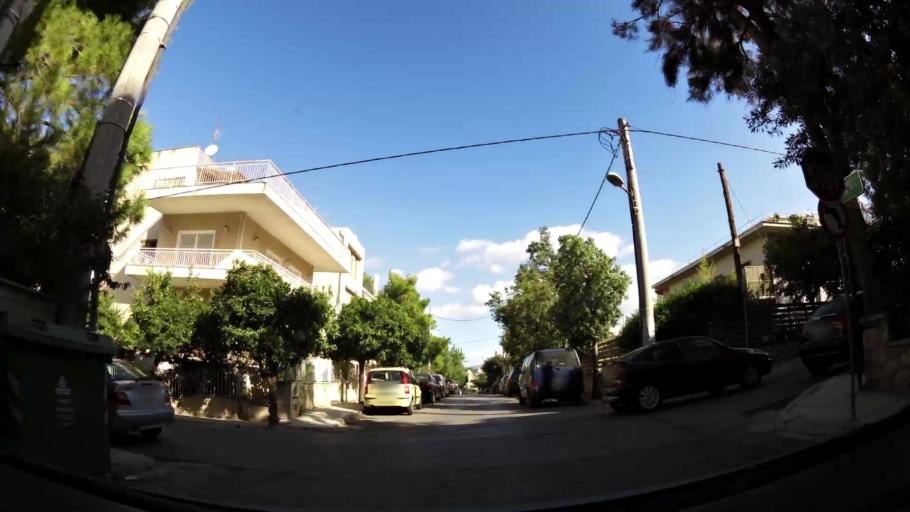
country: GR
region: Attica
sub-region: Nomarchia Athinas
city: Neo Psychiko
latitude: 38.0057
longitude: 23.7791
